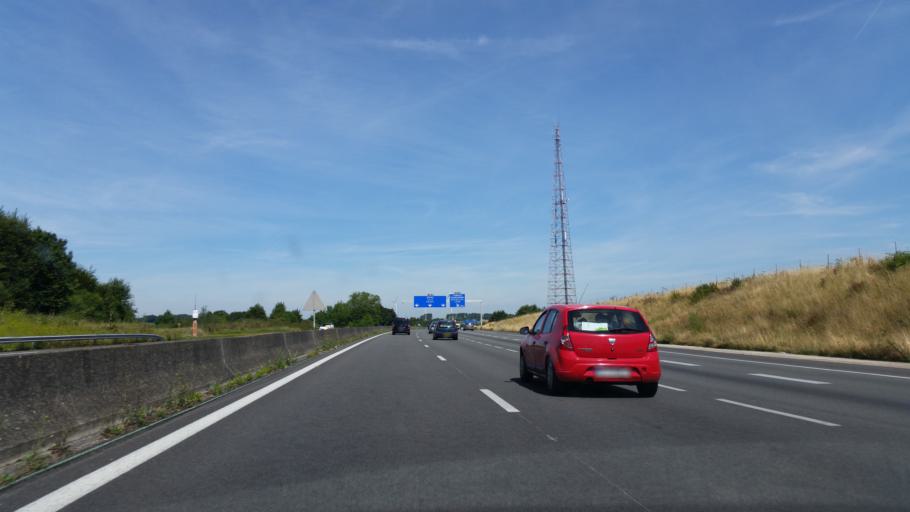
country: FR
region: Picardie
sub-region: Departement de la Somme
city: Moislains
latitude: 50.0076
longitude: 2.8767
